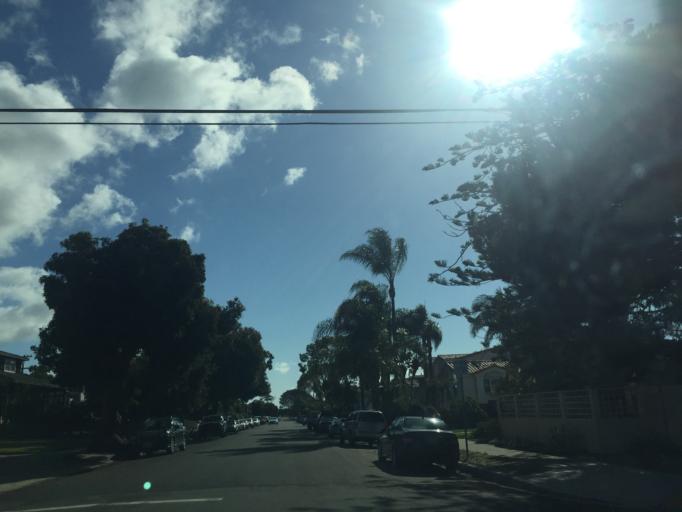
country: US
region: California
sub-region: San Diego County
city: La Jolla
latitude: 32.7920
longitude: -117.2405
